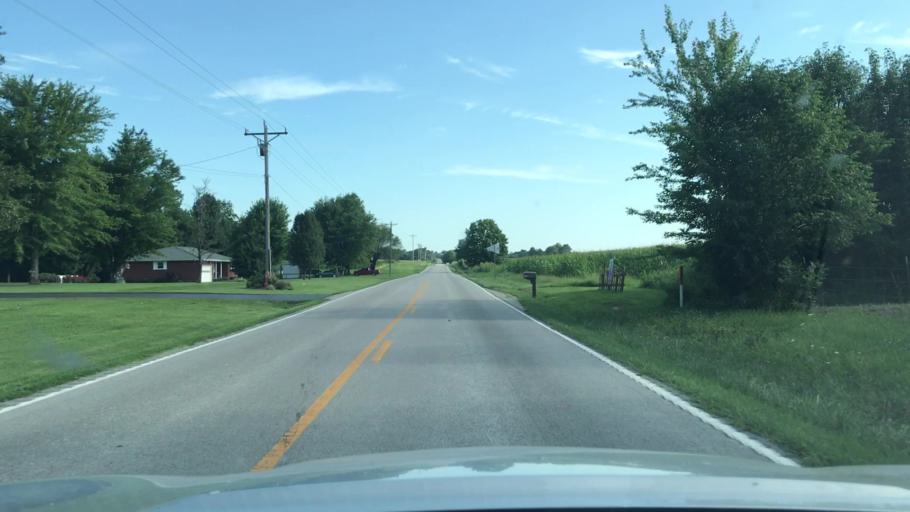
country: US
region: Kentucky
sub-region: Todd County
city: Elkton
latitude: 36.9161
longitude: -87.1631
